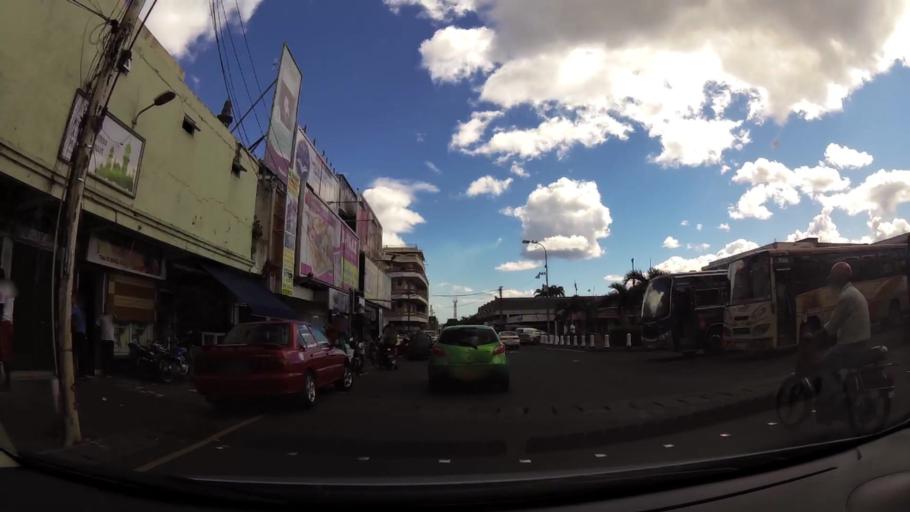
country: MU
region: Port Louis
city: Port Louis
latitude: -20.1592
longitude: 57.5114
